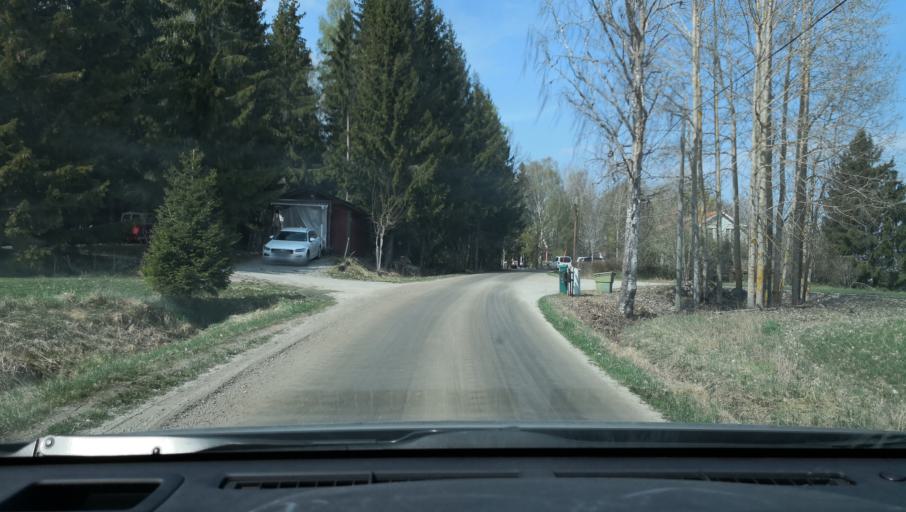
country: SE
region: Vaestmanland
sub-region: Vasteras
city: Skultuna
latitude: 59.7676
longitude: 16.4530
